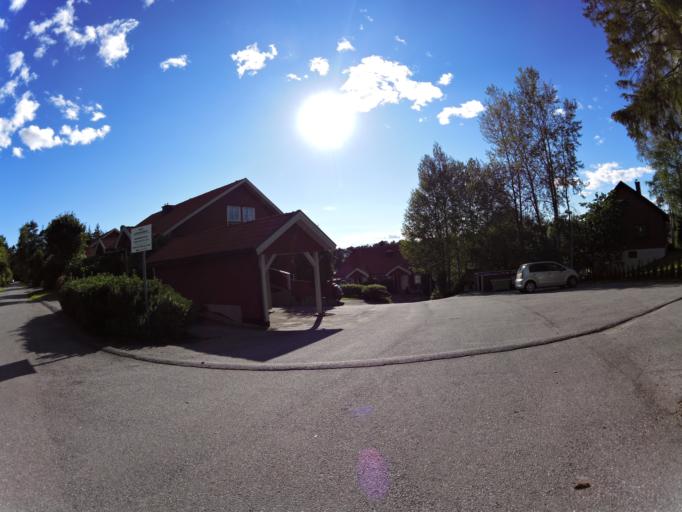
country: NO
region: Ostfold
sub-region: Fredrikstad
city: Fredrikstad
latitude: 59.2228
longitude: 10.9564
